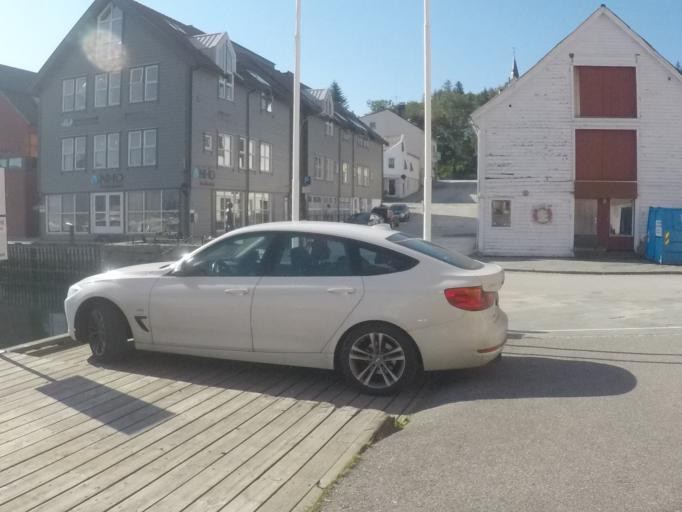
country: NO
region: Sogn og Fjordane
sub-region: Flora
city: Floro
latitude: 61.6006
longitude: 5.0296
